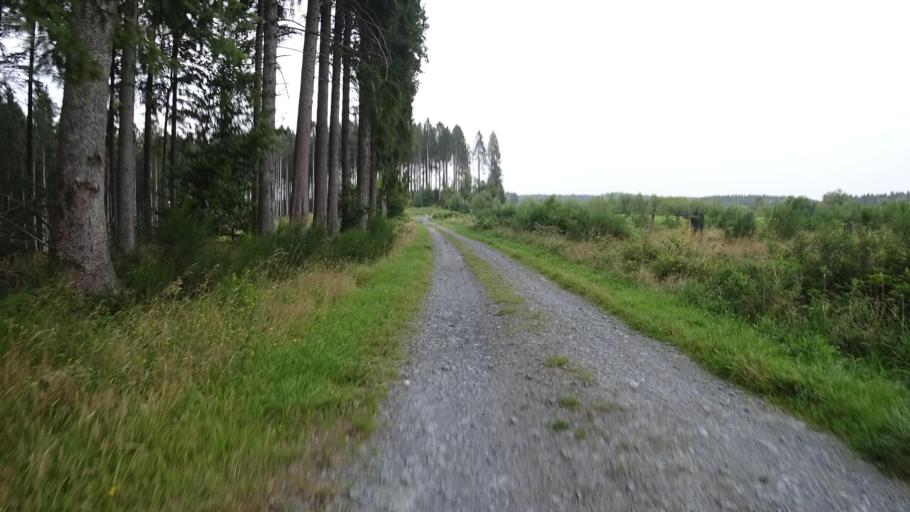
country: BE
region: Wallonia
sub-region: Province du Luxembourg
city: Chiny
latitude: 49.7891
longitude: 5.3244
